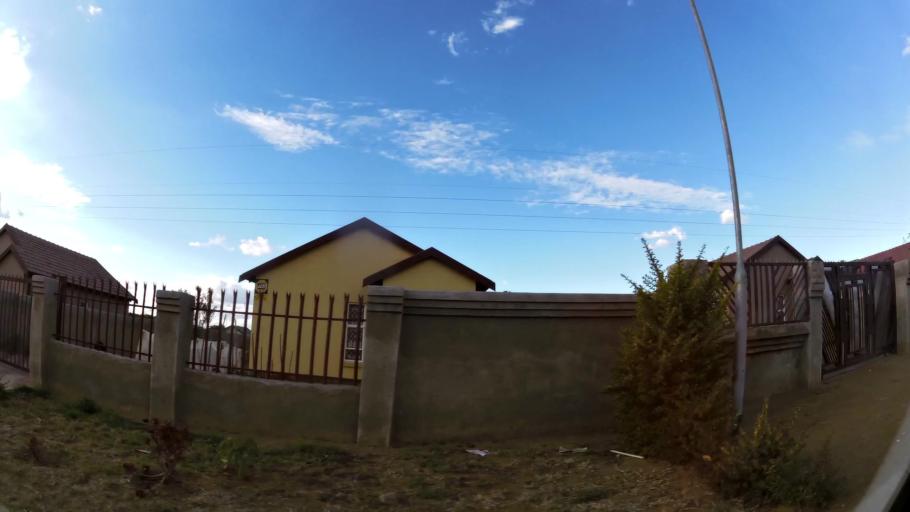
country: ZA
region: Limpopo
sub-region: Capricorn District Municipality
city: Polokwane
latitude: -23.9276
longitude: 29.4160
